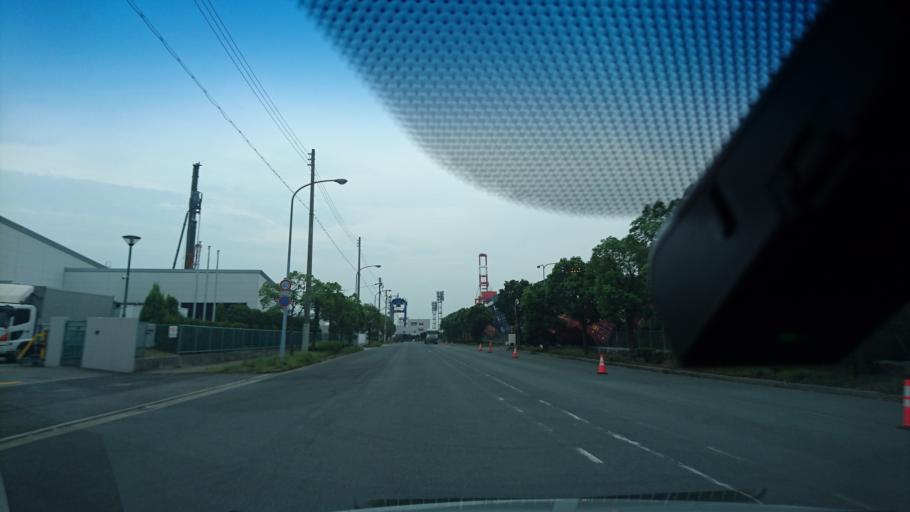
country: JP
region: Hyogo
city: Ashiya
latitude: 34.6837
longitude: 135.2578
